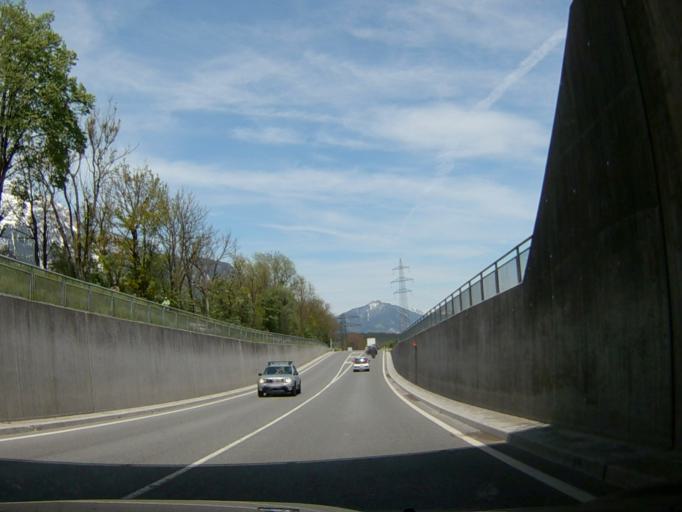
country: AT
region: Tyrol
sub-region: Politischer Bezirk Schwaz
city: Wiesing
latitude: 47.3918
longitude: 11.7968
